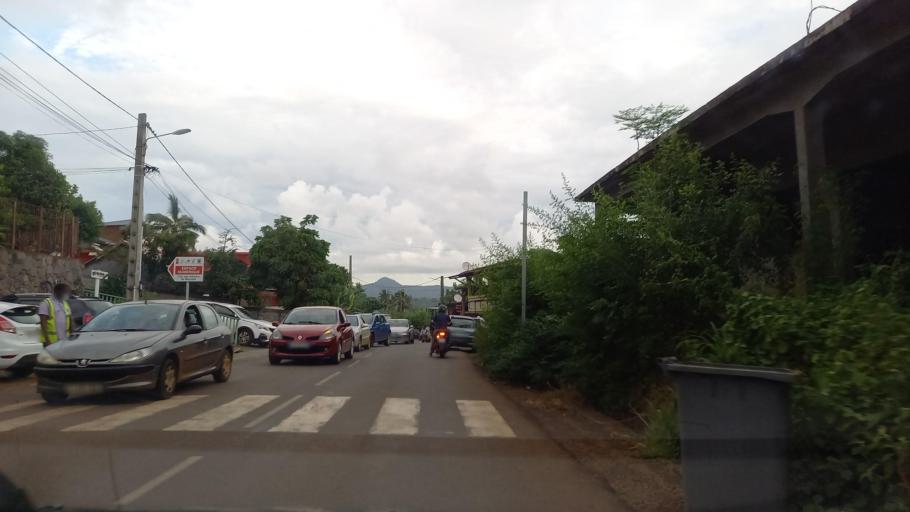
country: YT
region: M'Tsangamouji
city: M'Tsangamouji
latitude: -12.7656
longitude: 45.0770
